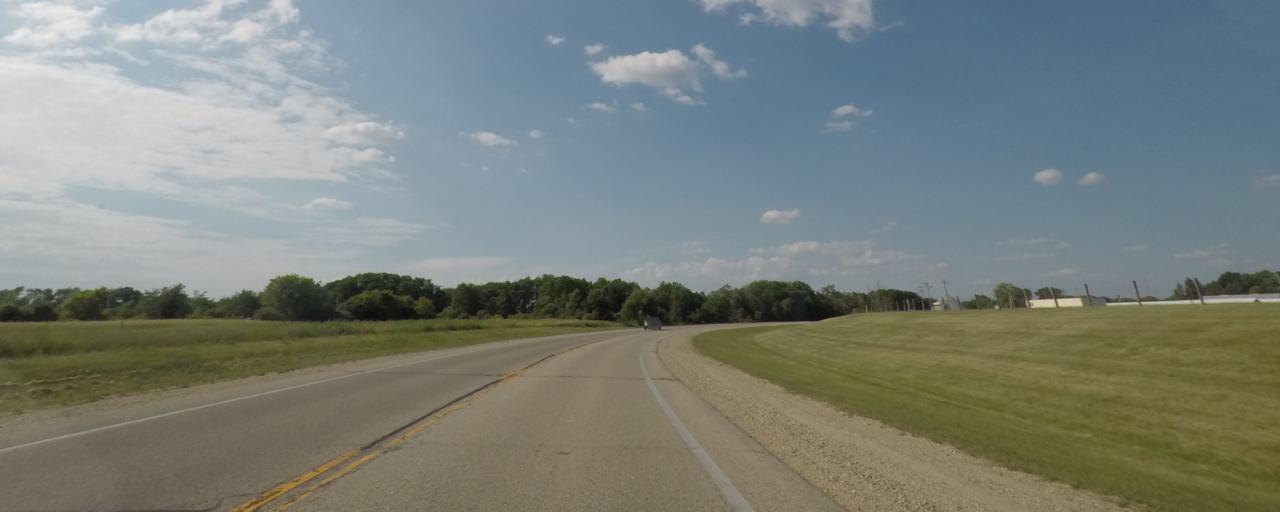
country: US
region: Wisconsin
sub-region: Walworth County
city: East Troy
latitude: 42.7957
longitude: -88.3814
